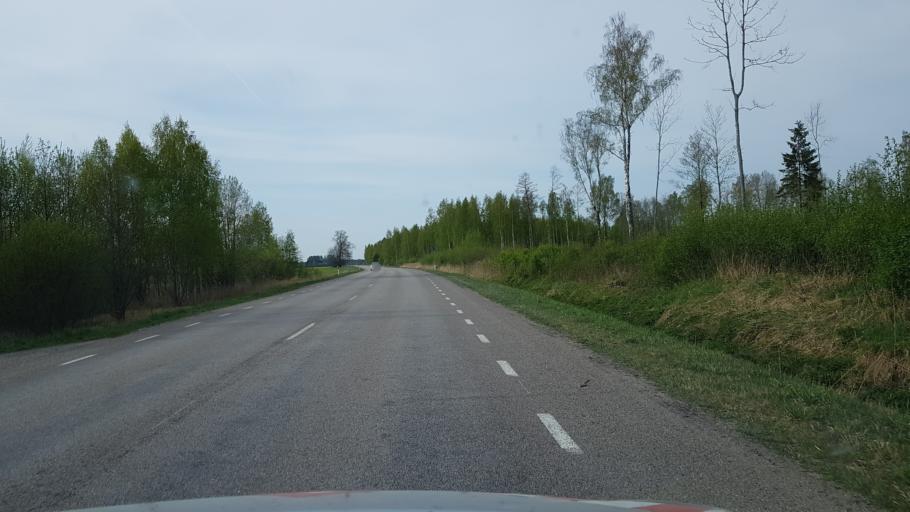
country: EE
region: Paernumaa
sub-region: Audru vald
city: Audru
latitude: 58.3869
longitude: 24.2734
